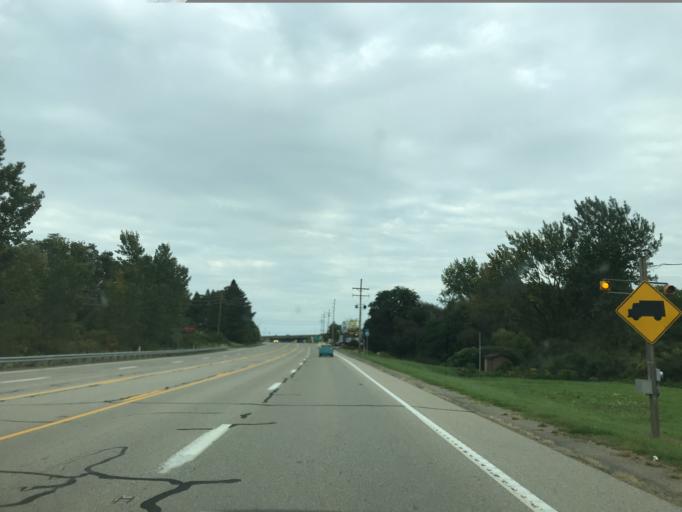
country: US
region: Pennsylvania
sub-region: Erie County
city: North East
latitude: 42.2311
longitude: -79.7859
